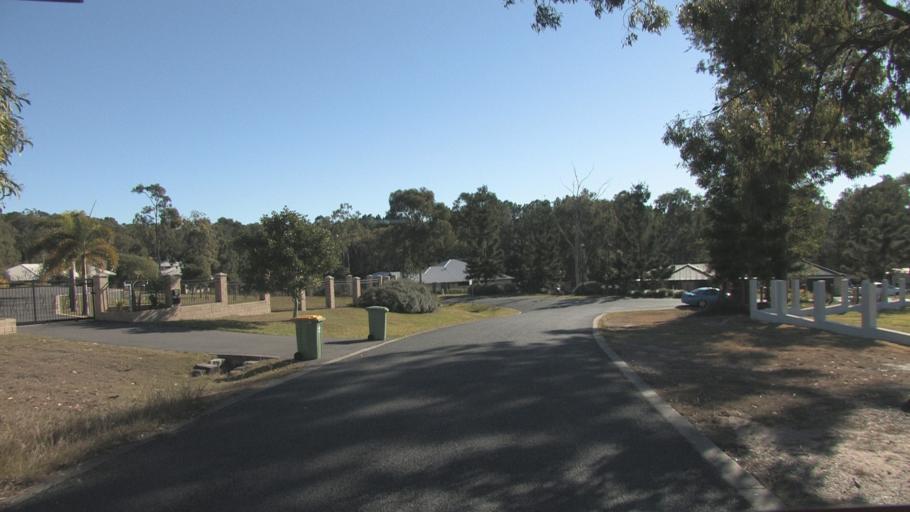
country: AU
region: Queensland
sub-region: Logan
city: North Maclean
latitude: -27.7471
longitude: 152.9583
